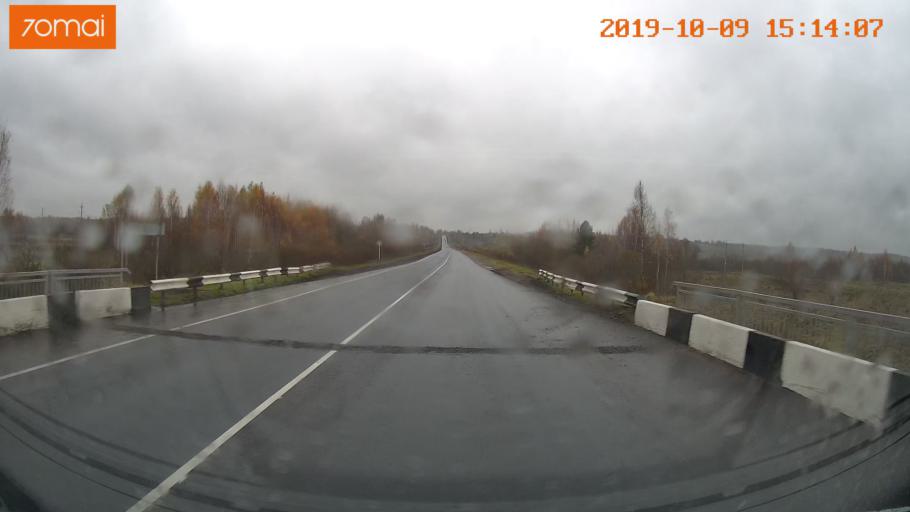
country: RU
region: Kostroma
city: Susanino
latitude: 58.1384
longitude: 41.6056
